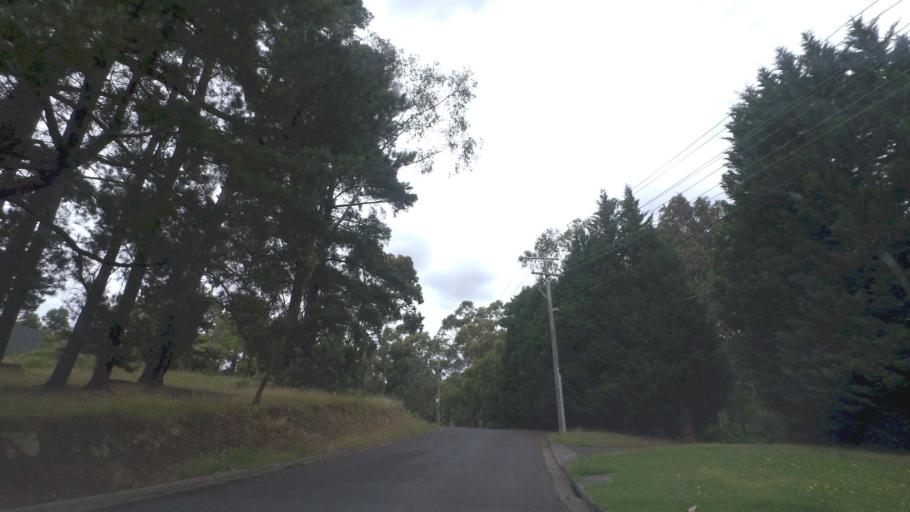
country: AU
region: Victoria
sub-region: Manningham
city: Park Orchards
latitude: -37.7850
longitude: 145.2189
